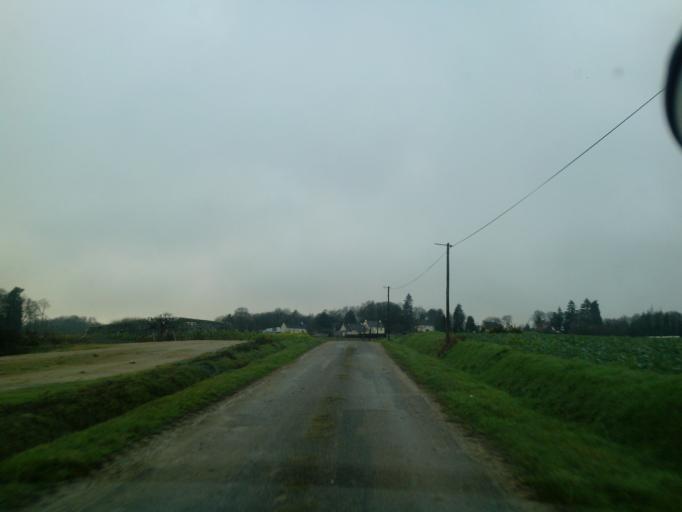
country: FR
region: Brittany
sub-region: Departement du Morbihan
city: Meneac
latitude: 48.1311
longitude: -2.4683
